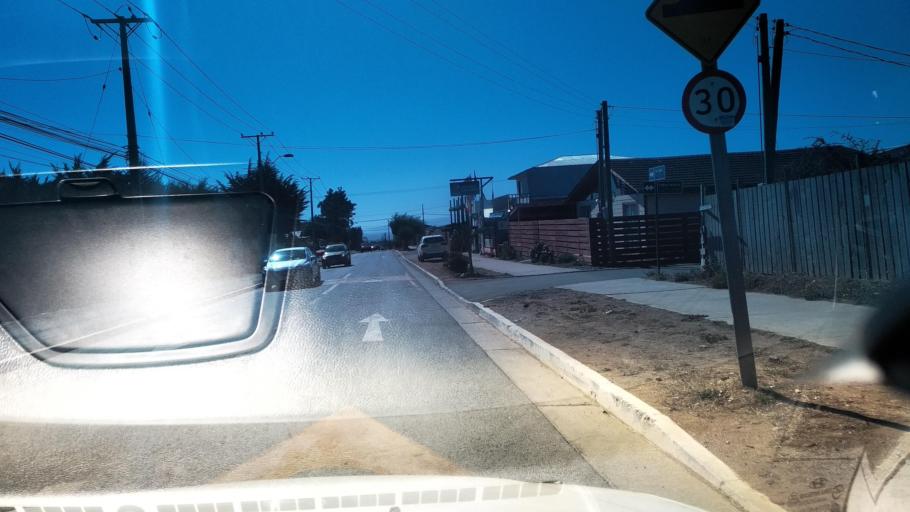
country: CL
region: O'Higgins
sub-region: Provincia de Colchagua
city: Santa Cruz
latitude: -34.4034
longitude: -71.9957
